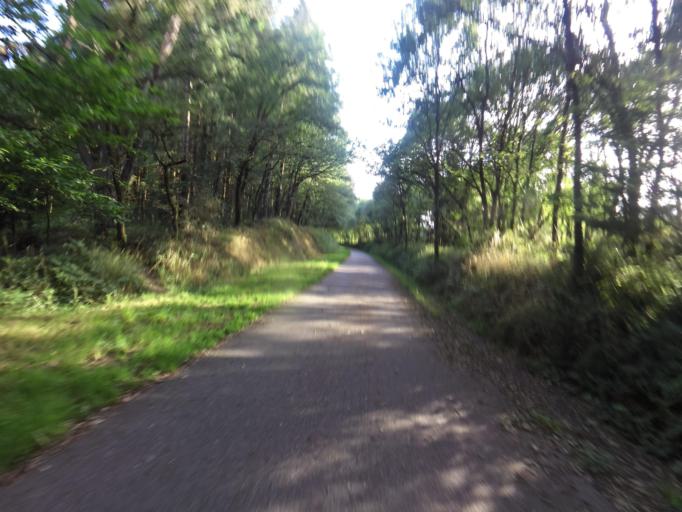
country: FR
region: Brittany
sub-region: Departement du Morbihan
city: Ploermel
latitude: 47.9214
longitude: -2.4239
